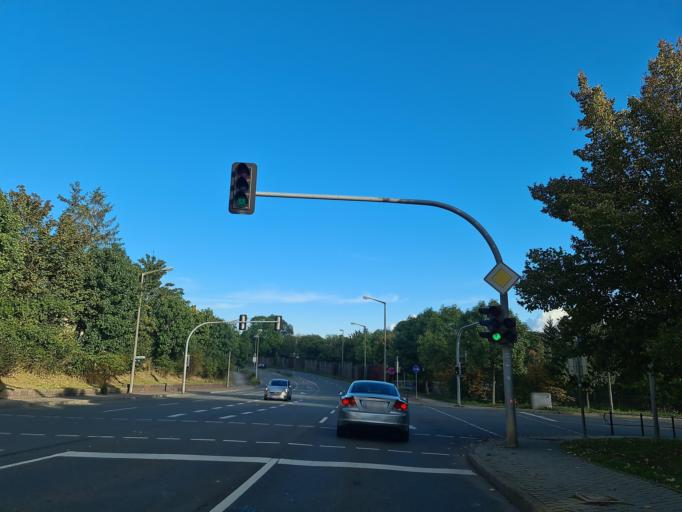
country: DE
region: Thuringia
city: Gera
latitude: 50.8810
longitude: 12.1065
